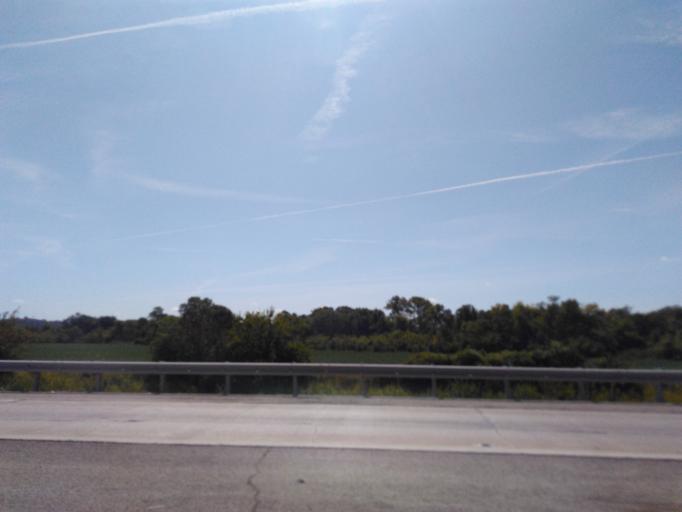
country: US
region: Illinois
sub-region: Saint Clair County
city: Washington Park
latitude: 38.6136
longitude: -90.0737
